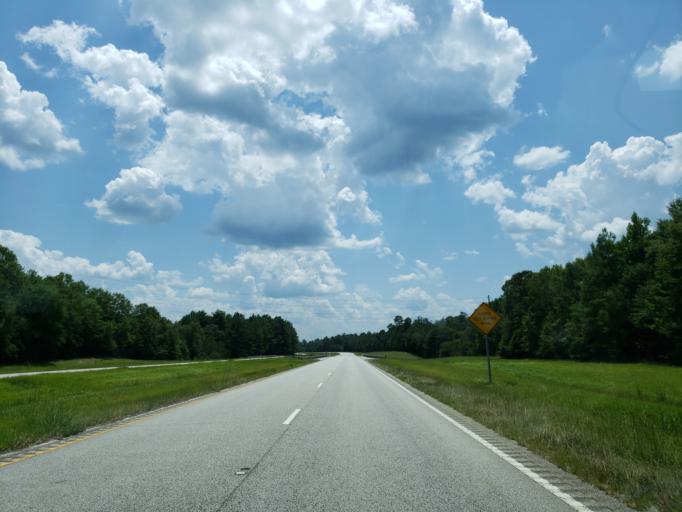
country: US
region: Mississippi
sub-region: Greene County
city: Leakesville
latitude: 31.2774
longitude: -88.5109
